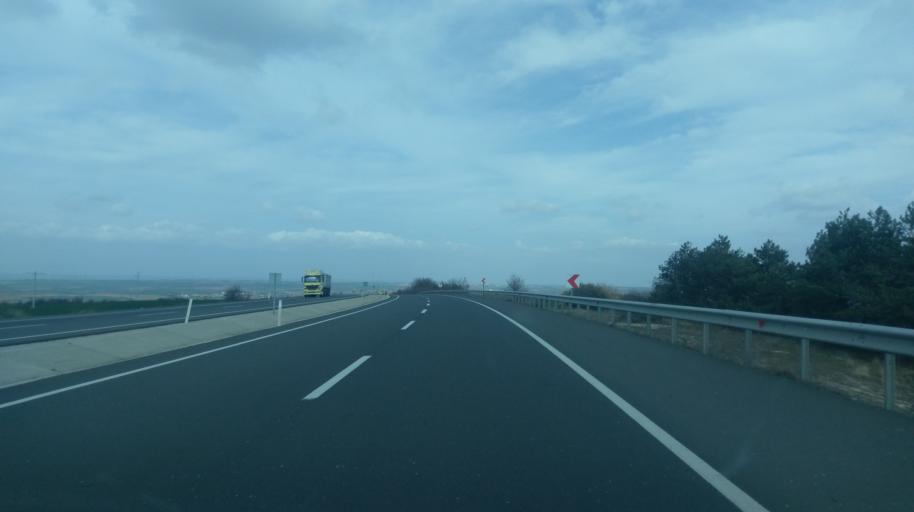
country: TR
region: Edirne
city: Hamidiye
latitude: 41.0805
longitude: 26.6393
